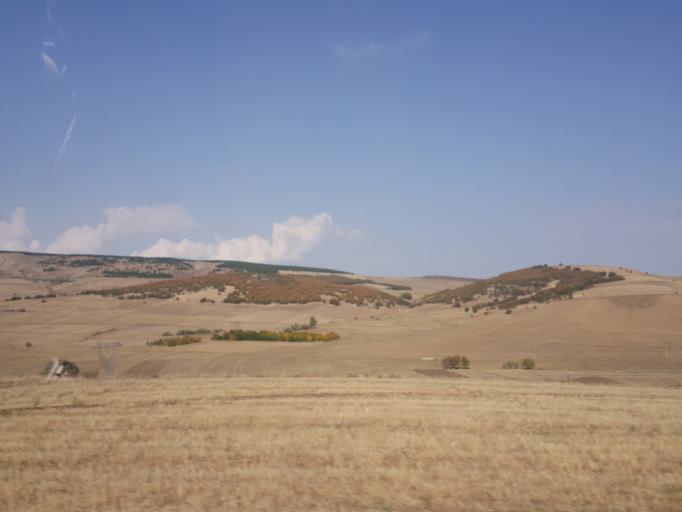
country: TR
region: Corum
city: Bogazkale
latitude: 40.1637
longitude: 34.6610
